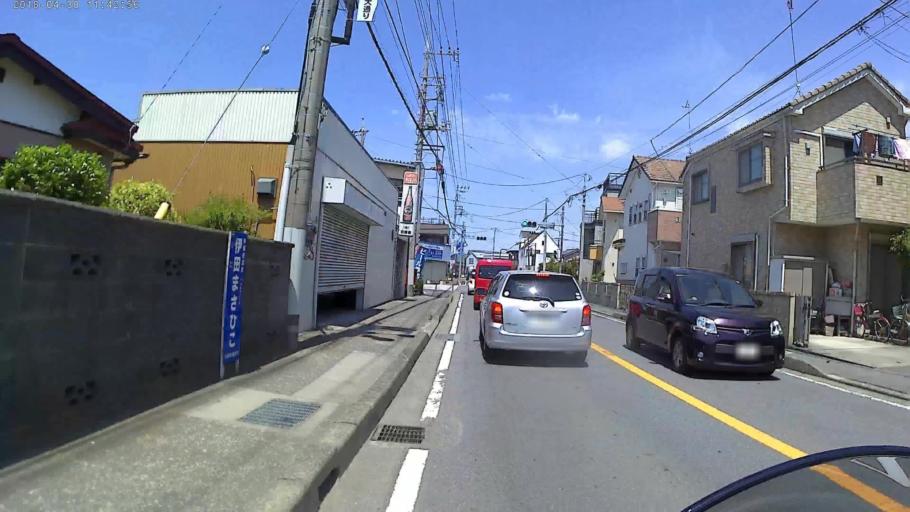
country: JP
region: Kanagawa
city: Zama
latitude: 35.4854
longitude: 139.3914
